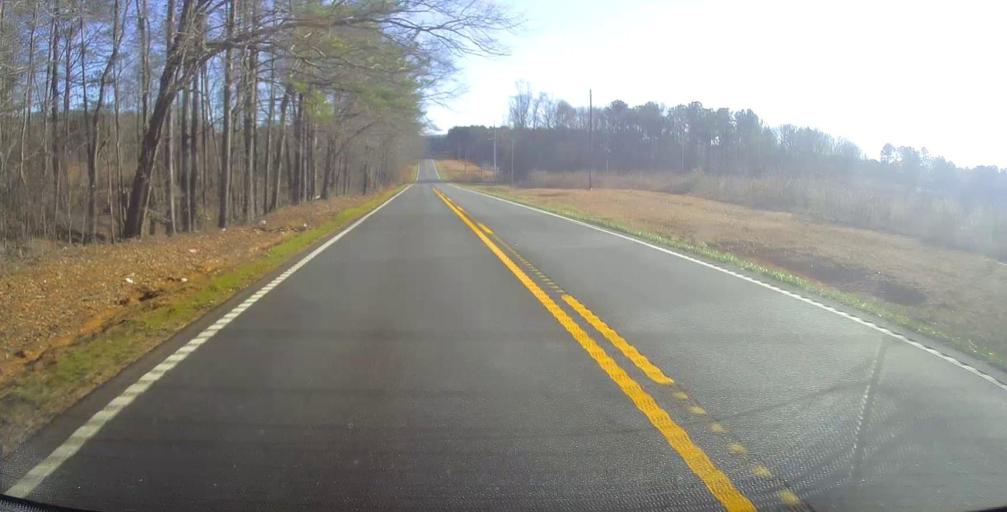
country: US
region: Georgia
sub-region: Talbot County
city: Sardis
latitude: 32.7951
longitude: -84.6927
